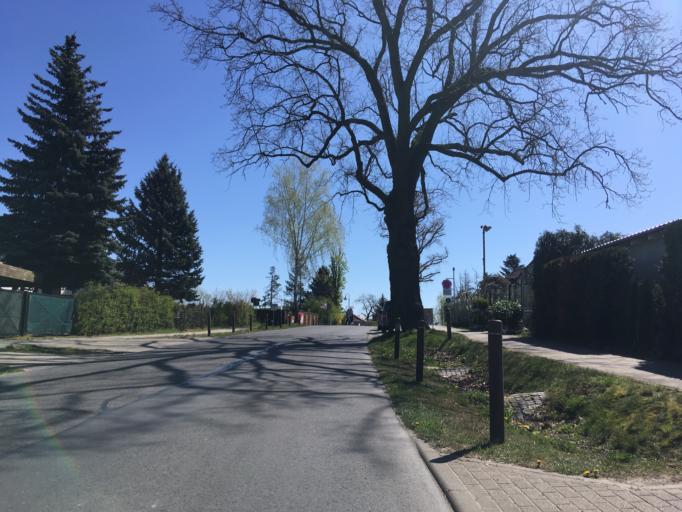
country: DE
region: Brandenburg
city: Bernau bei Berlin
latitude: 52.6444
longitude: 13.5569
